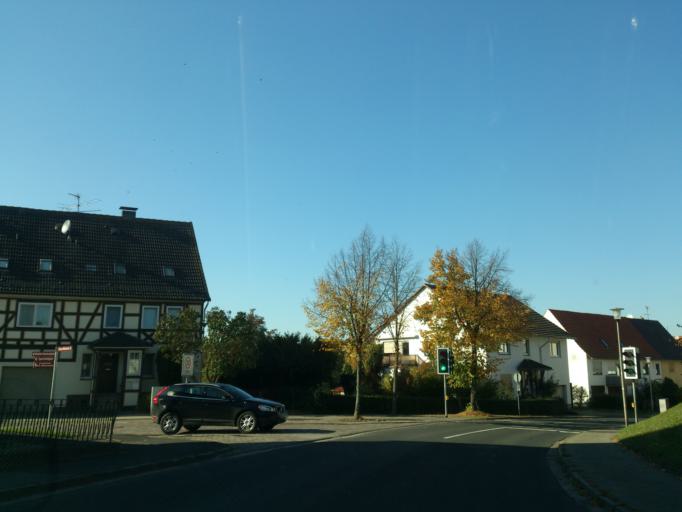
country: DE
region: Hesse
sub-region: Regierungsbezirk Kassel
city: Calden
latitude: 51.4047
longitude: 9.4026
